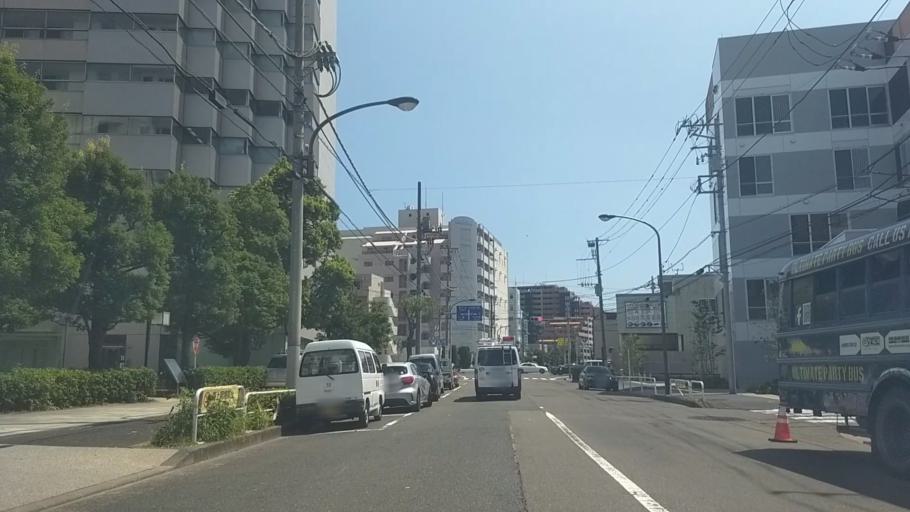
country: JP
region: Kanagawa
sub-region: Kawasaki-shi
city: Kawasaki
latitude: 35.6077
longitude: 139.7453
